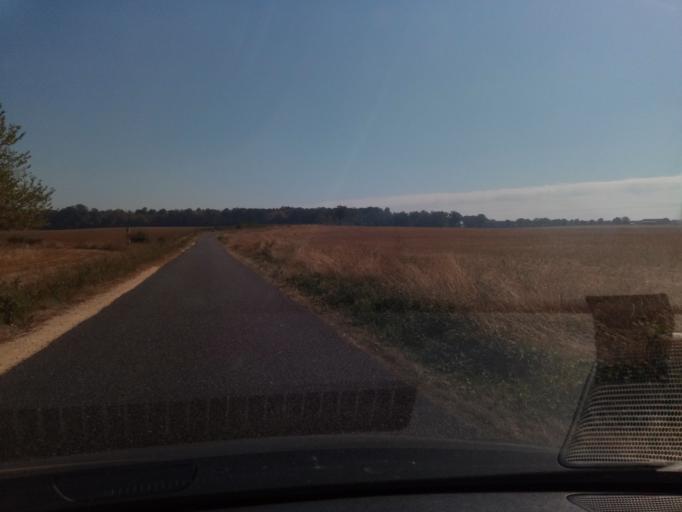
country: FR
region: Poitou-Charentes
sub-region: Departement de la Vienne
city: Lussac-les-Chateaux
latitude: 46.3820
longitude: 0.7851
